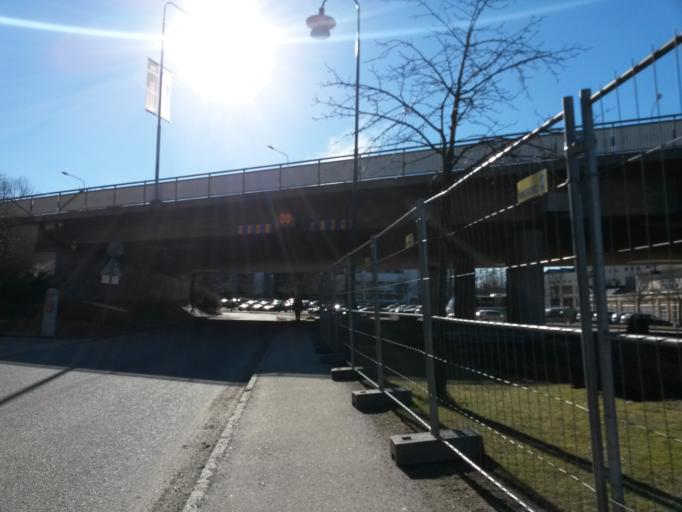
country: SE
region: Vaestra Goetaland
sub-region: Boras Kommun
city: Boras
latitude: 57.7266
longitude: 12.9401
